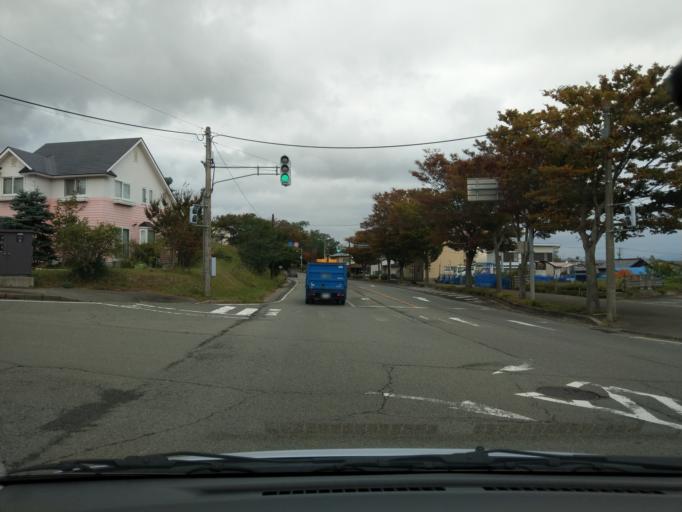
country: JP
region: Akita
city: Akita Shi
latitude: 39.6771
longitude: 140.0783
